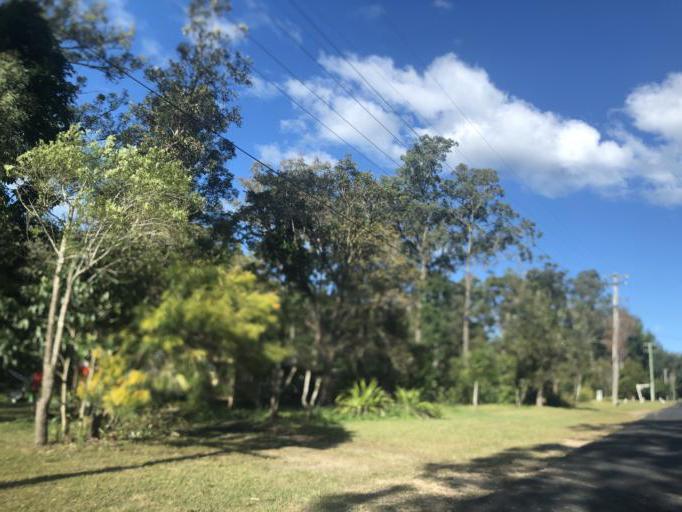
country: AU
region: New South Wales
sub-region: Coffs Harbour
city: Nana Glen
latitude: -30.0548
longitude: 152.9854
